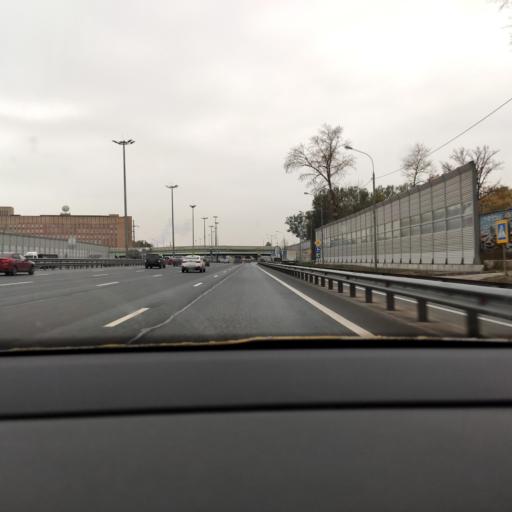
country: RU
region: Moskovskaya
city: Bolshevo
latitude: 55.9341
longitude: 37.8074
